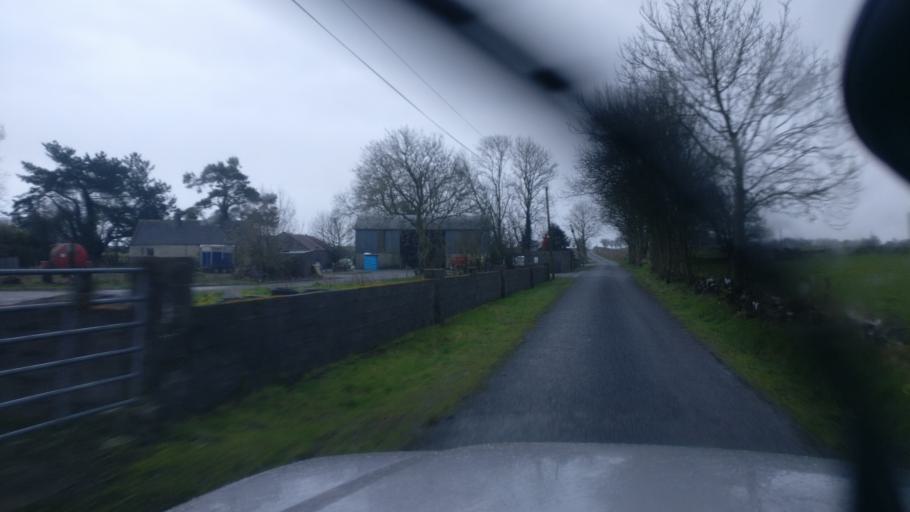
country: IE
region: Connaught
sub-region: County Galway
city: Loughrea
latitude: 53.2336
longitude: -8.4231
